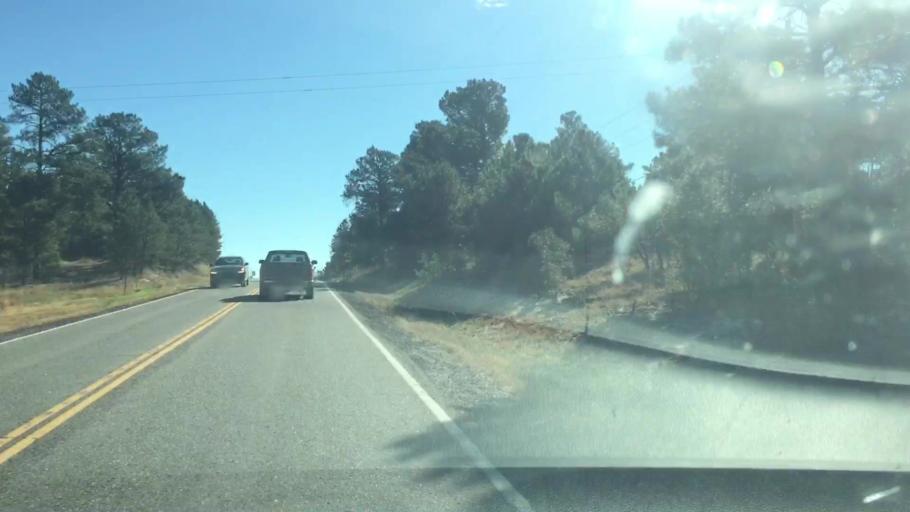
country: US
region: Colorado
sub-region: Elbert County
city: Elizabeth
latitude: 39.3615
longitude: -104.5741
